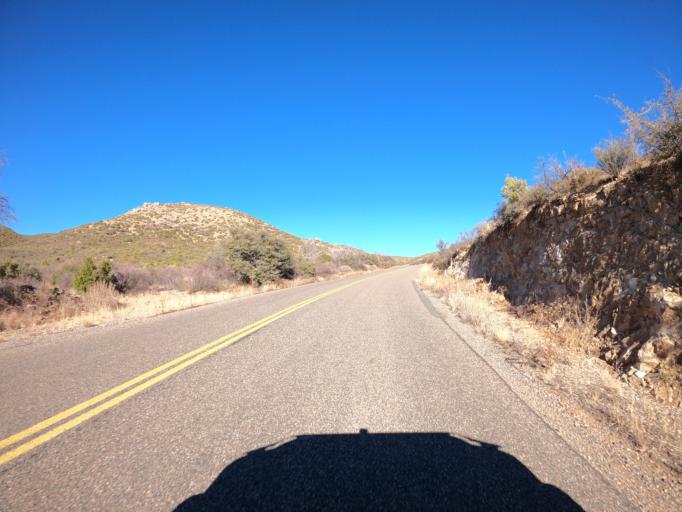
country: US
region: Arizona
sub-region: Yavapai County
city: Verde Village
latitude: 34.5633
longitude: -112.0765
